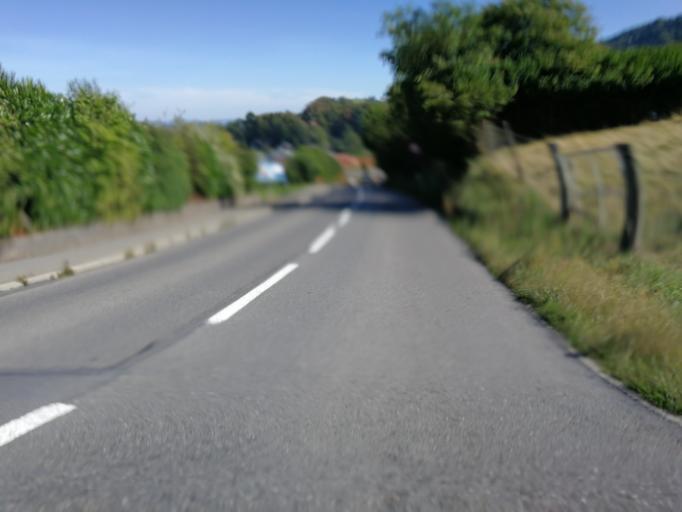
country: CH
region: Lucerne
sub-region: Lucerne-Land District
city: Weggis
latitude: 47.0519
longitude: 8.4284
